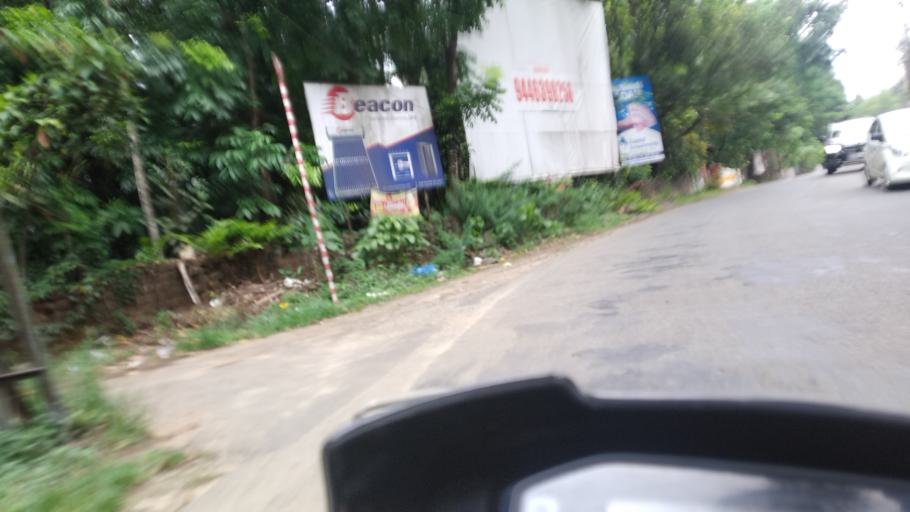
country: IN
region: Kerala
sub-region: Ernakulam
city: Perumpavur
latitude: 10.1079
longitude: 76.5363
